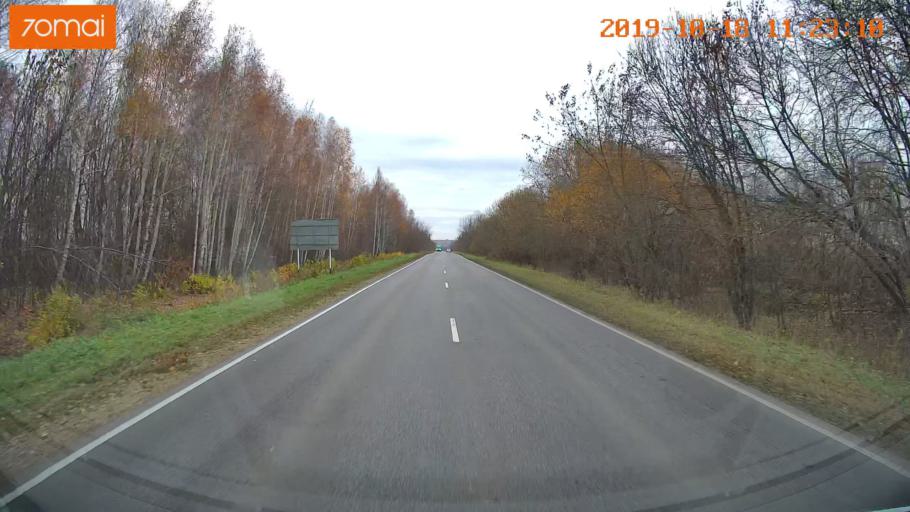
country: RU
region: Tula
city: Kimovsk
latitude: 54.0977
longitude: 38.5904
